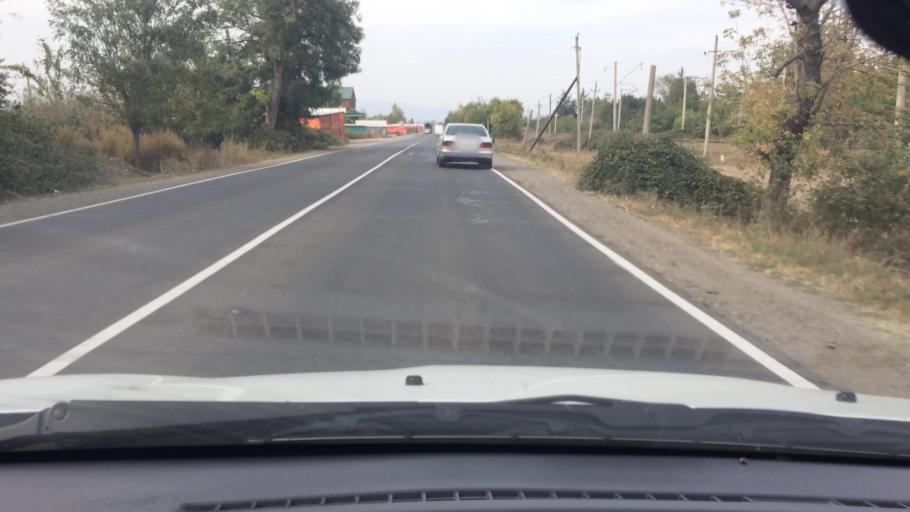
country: GE
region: Kvemo Kartli
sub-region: Marneuli
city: Marneuli
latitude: 41.4168
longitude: 44.8264
